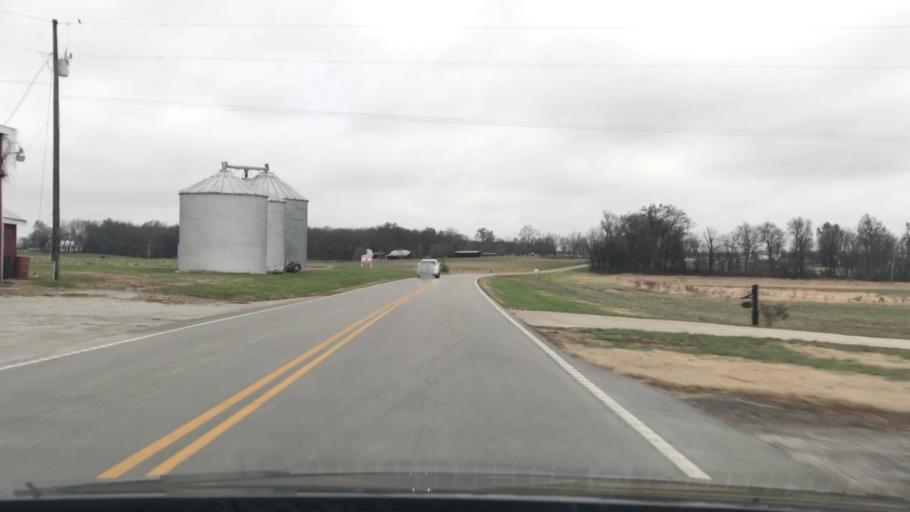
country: US
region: Kentucky
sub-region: Todd County
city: Elkton
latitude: 36.7331
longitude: -87.1889
